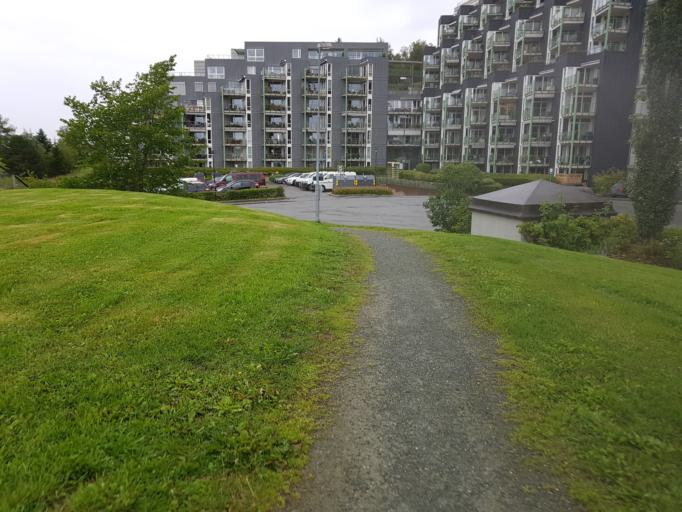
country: NO
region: Sor-Trondelag
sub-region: Trondheim
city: Trondheim
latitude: 63.4087
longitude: 10.4562
